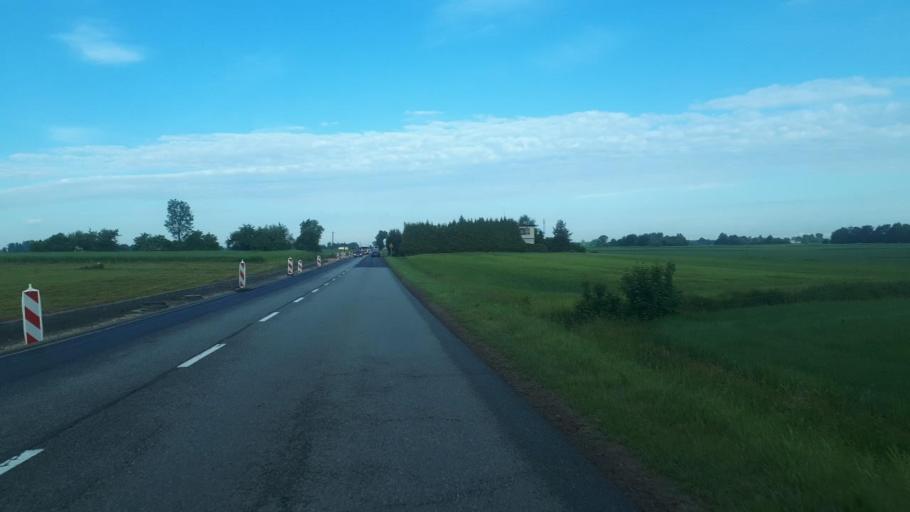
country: PL
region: Silesian Voivodeship
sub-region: Powiat pszczynski
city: Jankowice
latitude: 49.9707
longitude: 19.0119
